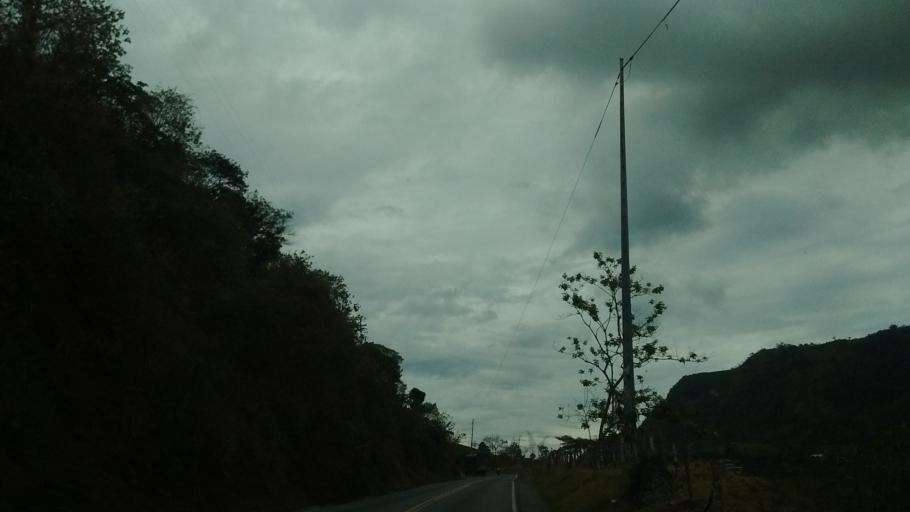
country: CO
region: Cauca
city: Rosas
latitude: 2.2678
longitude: -76.7330
